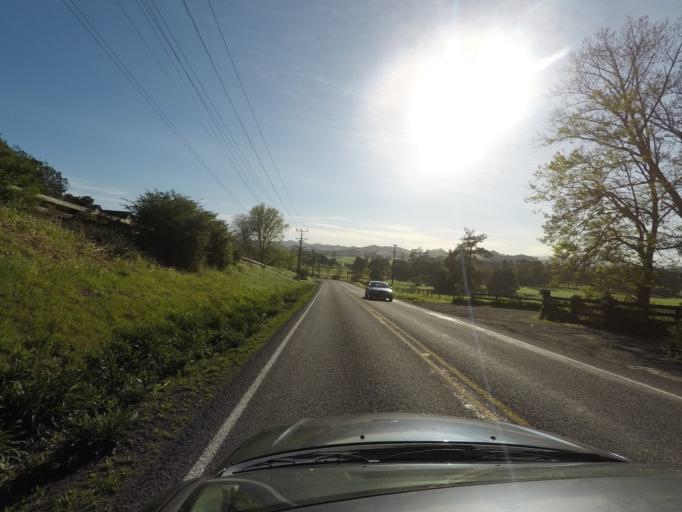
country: NZ
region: Auckland
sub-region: Auckland
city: Red Hill
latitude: -37.0131
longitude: 174.9488
